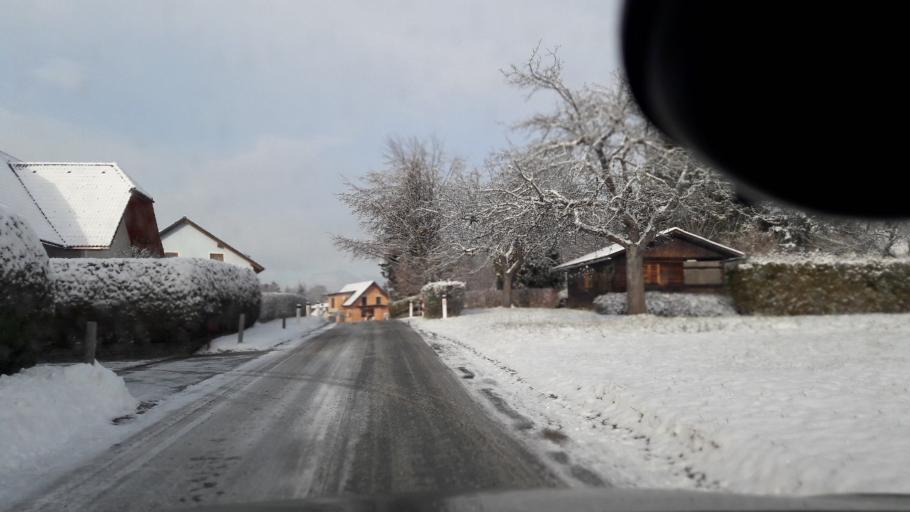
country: AT
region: Styria
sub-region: Politischer Bezirk Graz-Umgebung
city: Sankt Oswald bei Plankenwarth
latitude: 47.0909
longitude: 15.2637
